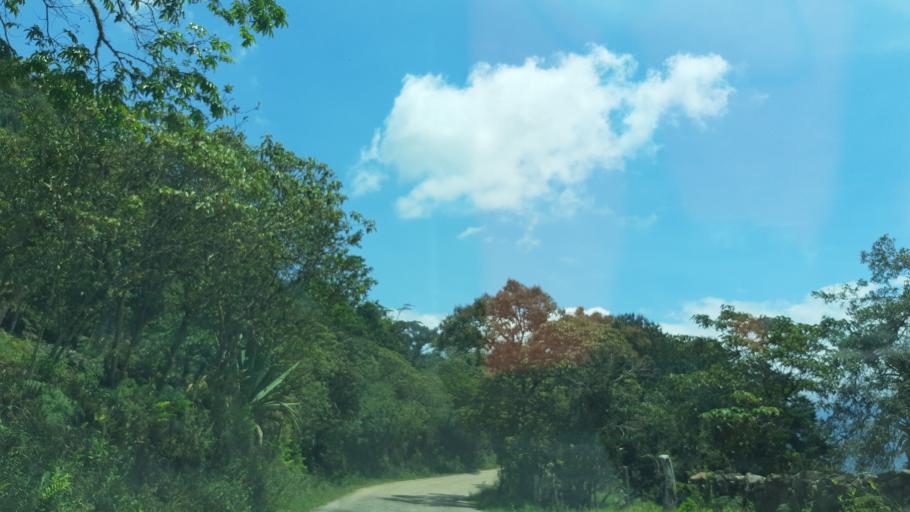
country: CO
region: Boyaca
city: Chinavita
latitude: 5.1239
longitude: -73.3858
